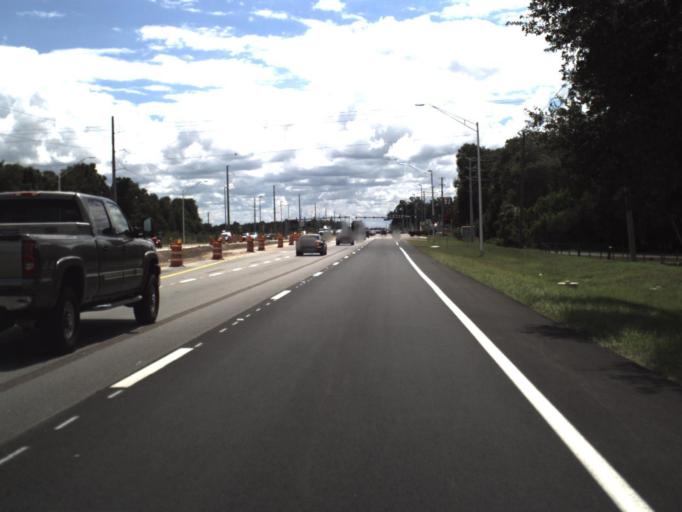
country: US
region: Florida
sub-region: Polk County
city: Highland City
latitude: 27.9559
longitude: -81.8721
